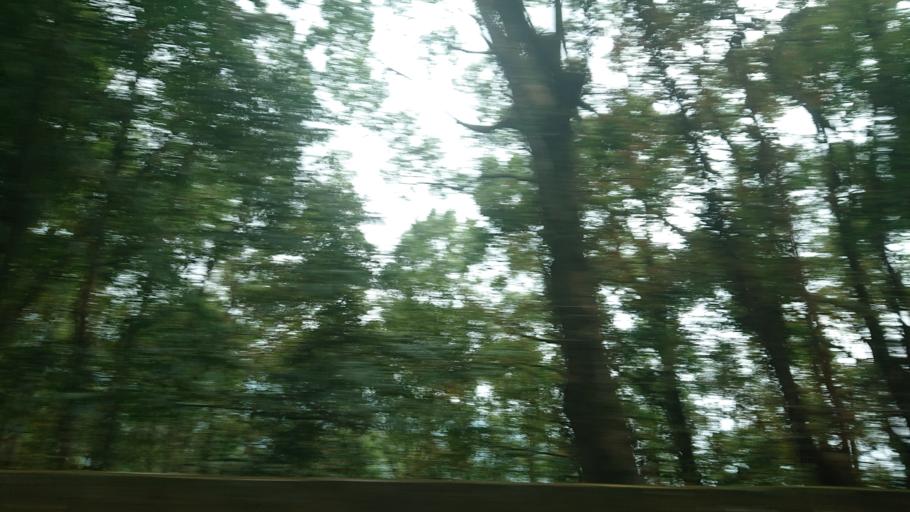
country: TW
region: Taiwan
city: Lugu
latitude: 23.6015
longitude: 120.7048
